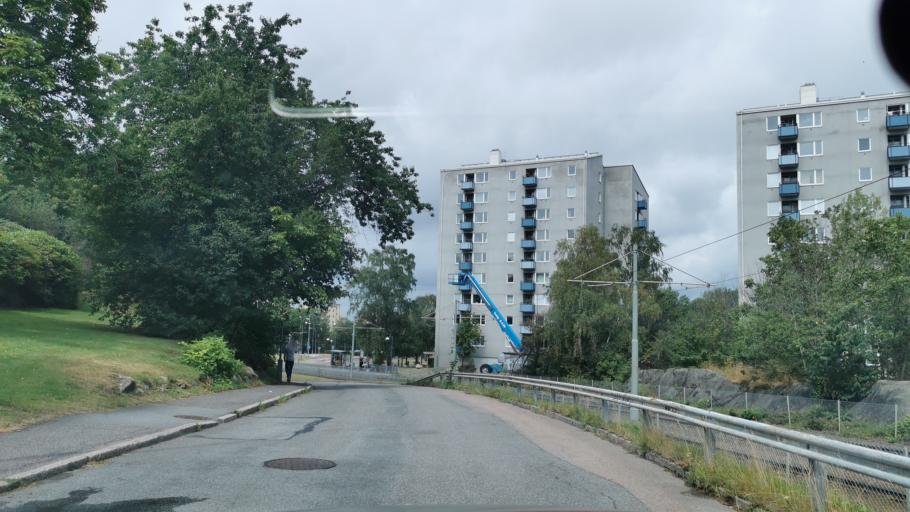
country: SE
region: Vaestra Goetaland
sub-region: Goteborg
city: Goeteborg
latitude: 57.6835
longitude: 11.9743
